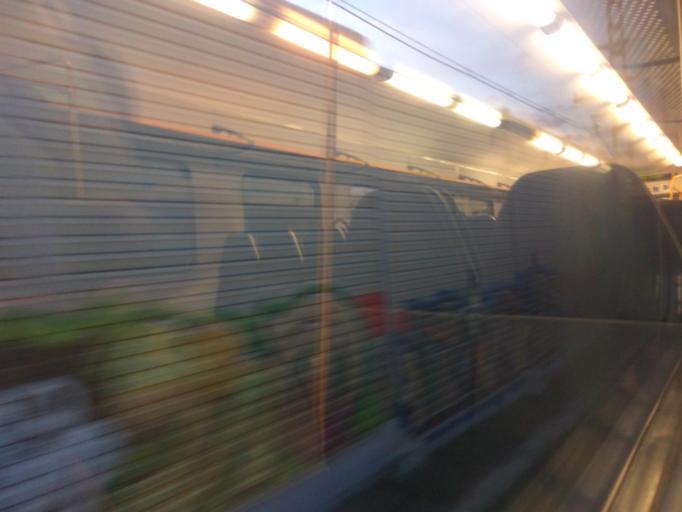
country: RU
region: Moscow
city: Solntsevo
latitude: 55.6530
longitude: 37.3807
